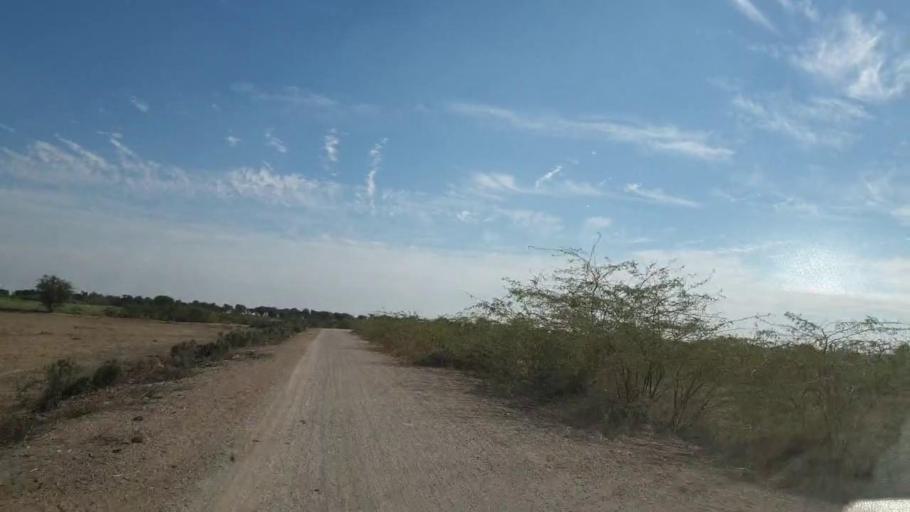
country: PK
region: Sindh
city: Pithoro
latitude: 25.5517
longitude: 69.2994
